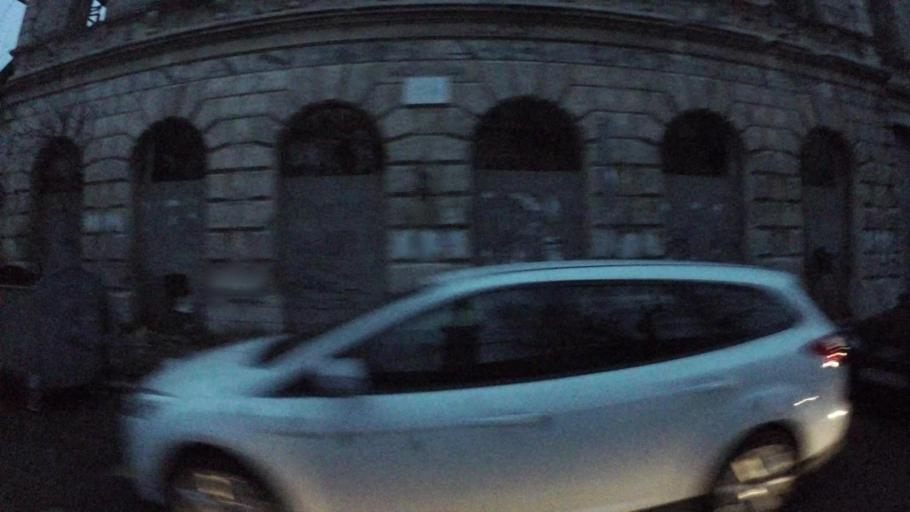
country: BA
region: Federation of Bosnia and Herzegovina
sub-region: Hercegovacko-Bosanski Kanton
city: Mostar
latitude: 43.3371
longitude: 17.8160
